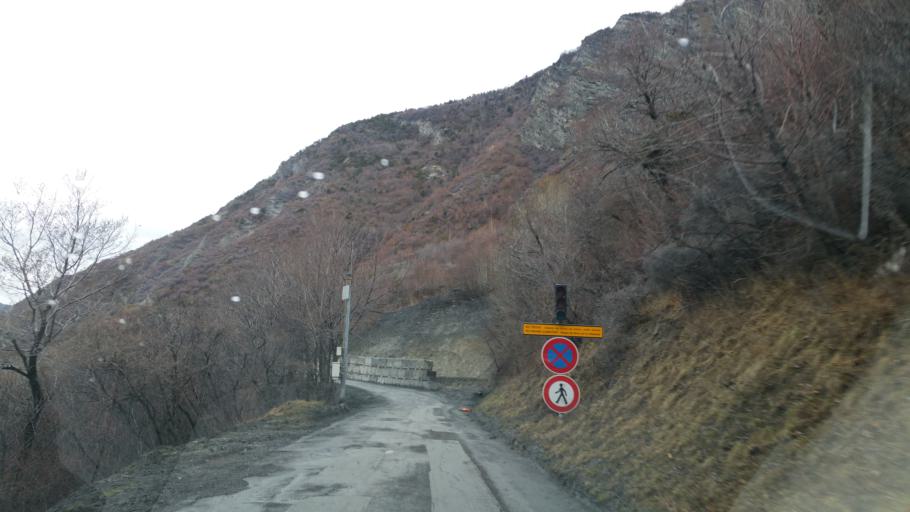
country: FR
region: Rhone-Alpes
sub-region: Departement de la Savoie
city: Villargondran
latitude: 45.2624
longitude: 6.3936
